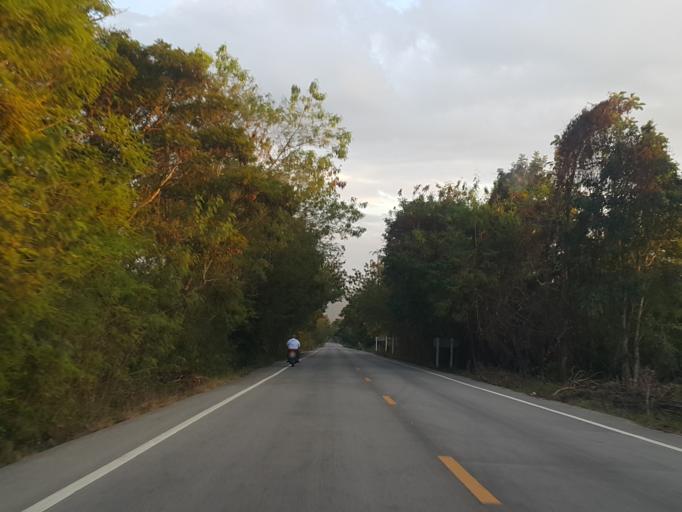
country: TH
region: Lampang
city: Mae Mo
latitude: 18.4337
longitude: 99.6418
